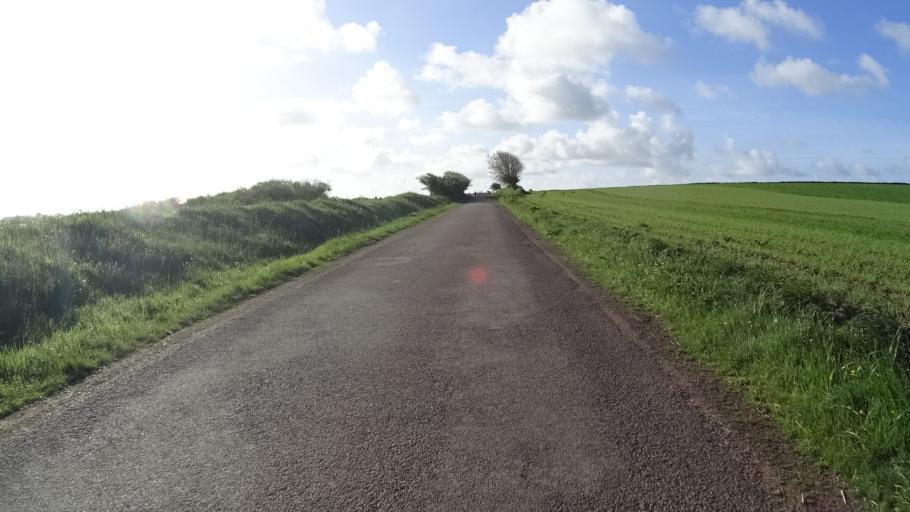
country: FR
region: Brittany
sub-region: Departement du Finistere
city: Ploumoguer
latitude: 48.4225
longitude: -4.6992
